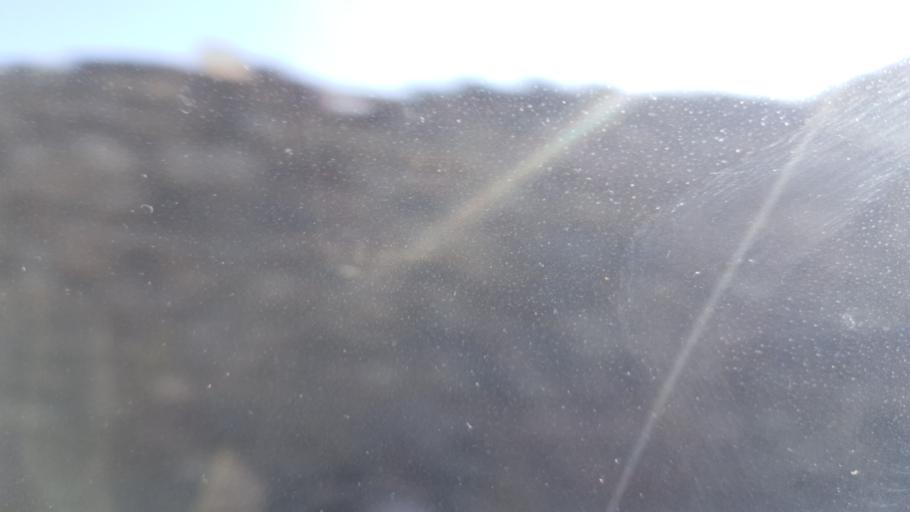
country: TR
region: Ankara
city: Yenice
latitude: 39.2743
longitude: 32.6746
